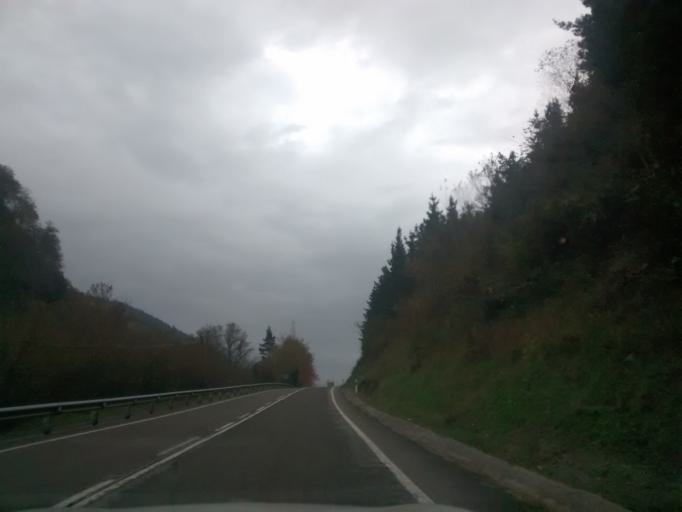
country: ES
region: Cantabria
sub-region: Provincia de Cantabria
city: San Pedro del Romeral
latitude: 43.1331
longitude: -3.9000
